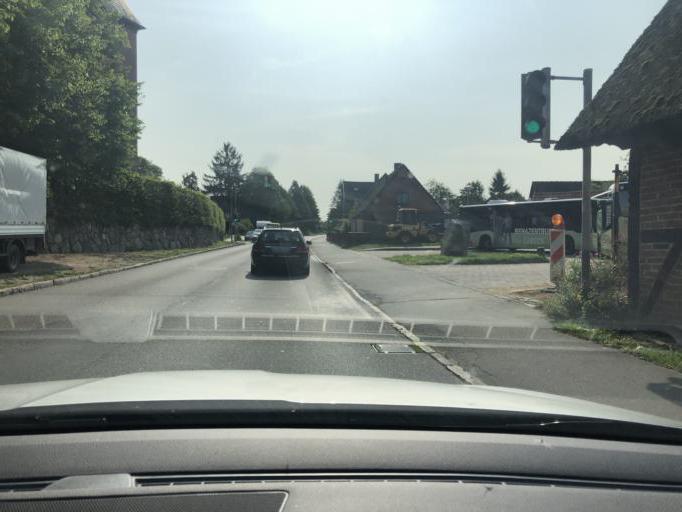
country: DE
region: Schleswig-Holstein
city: Gross Gronau
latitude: 53.7987
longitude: 10.7536
